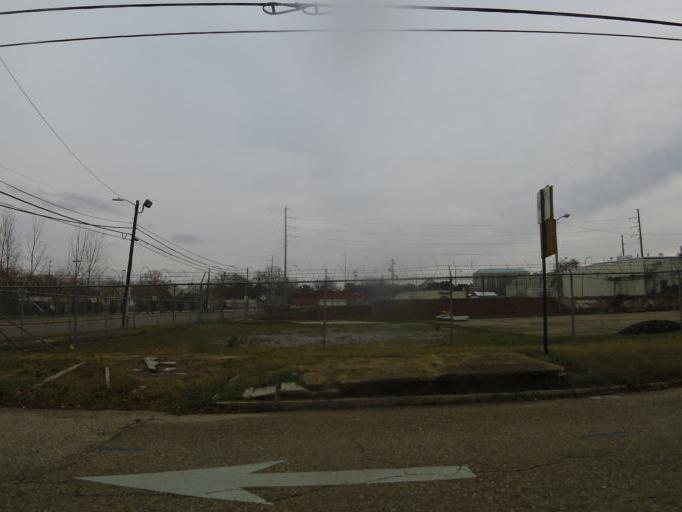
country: US
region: Alabama
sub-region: Montgomery County
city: Montgomery
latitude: 32.3819
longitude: -86.3076
